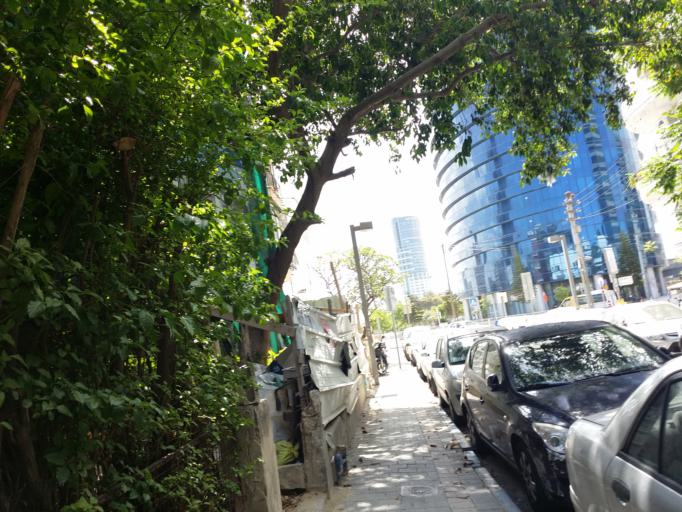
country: IL
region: Tel Aviv
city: Tel Aviv
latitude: 32.0644
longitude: 34.7805
